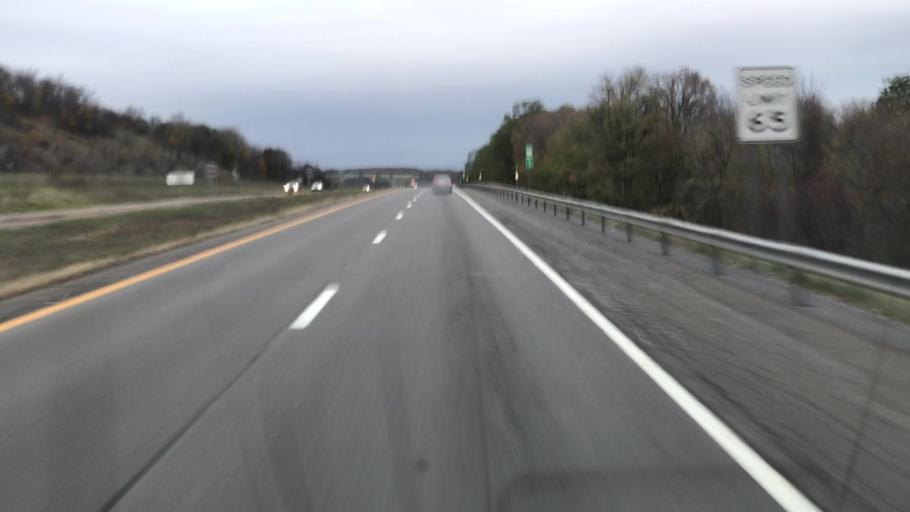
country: US
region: New York
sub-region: Onondaga County
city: Camillus
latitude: 43.0377
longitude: -76.3196
